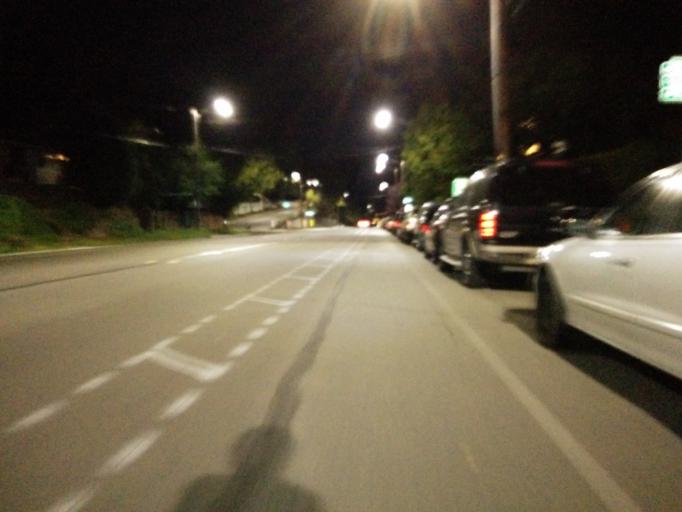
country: US
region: Washington
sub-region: King County
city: Seattle
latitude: 47.6397
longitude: -122.3442
